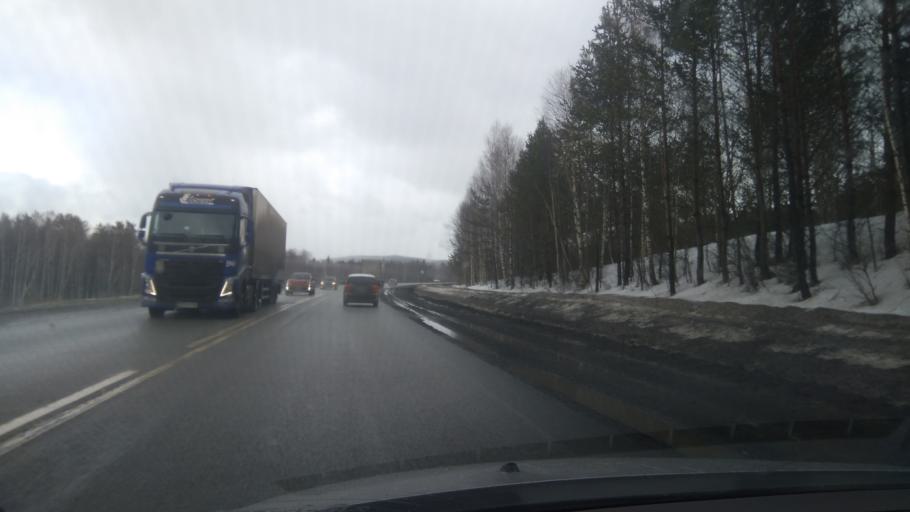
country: RU
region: Sverdlovsk
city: Ufimskiy
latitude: 56.7860
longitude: 58.3886
